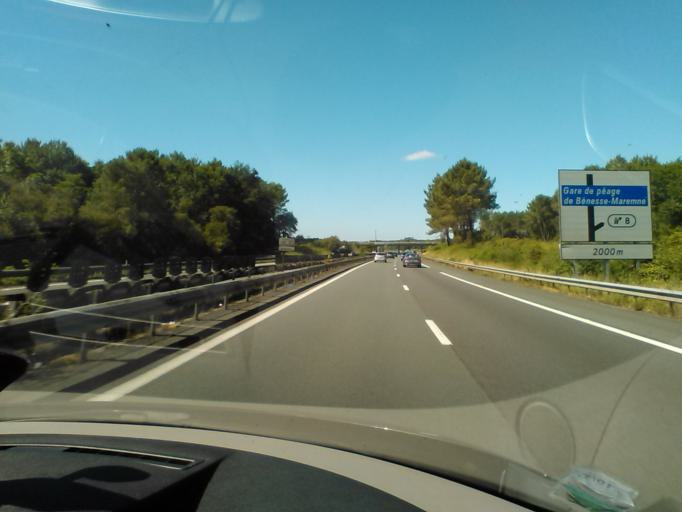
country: FR
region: Aquitaine
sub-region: Departement des Landes
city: Angresse
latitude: 43.6445
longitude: -1.3726
